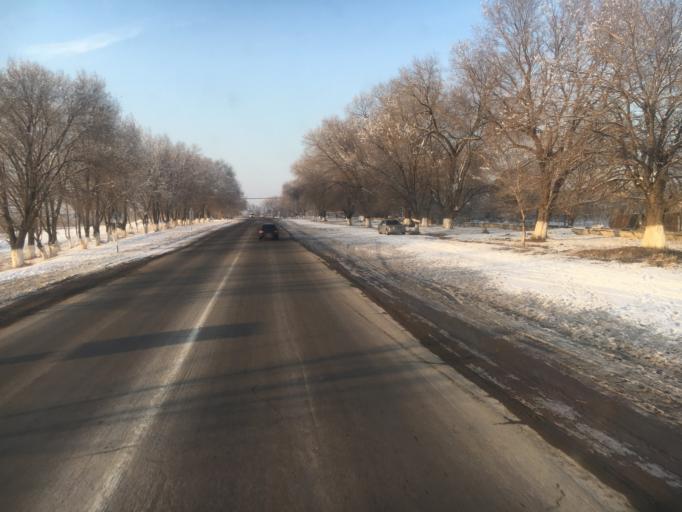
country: KZ
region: Almaty Oblysy
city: Burunday
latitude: 43.3378
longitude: 76.6595
